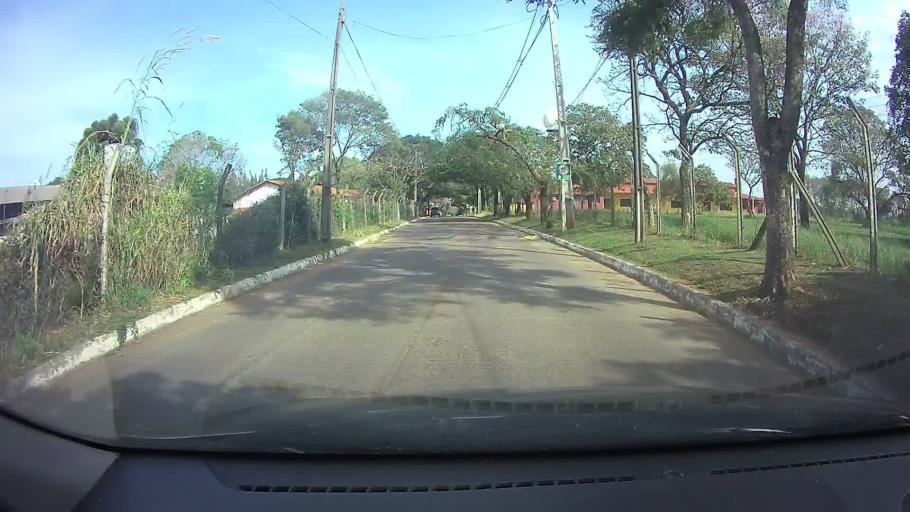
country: PY
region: Central
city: Fernando de la Mora
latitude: -25.3330
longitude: -57.5220
